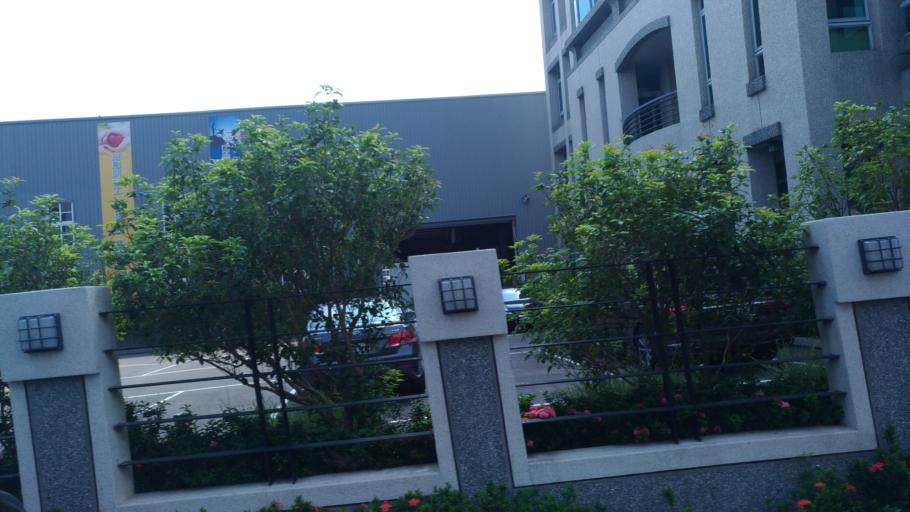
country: TW
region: Taiwan
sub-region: Yunlin
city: Douliu
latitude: 23.7573
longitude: 120.5042
